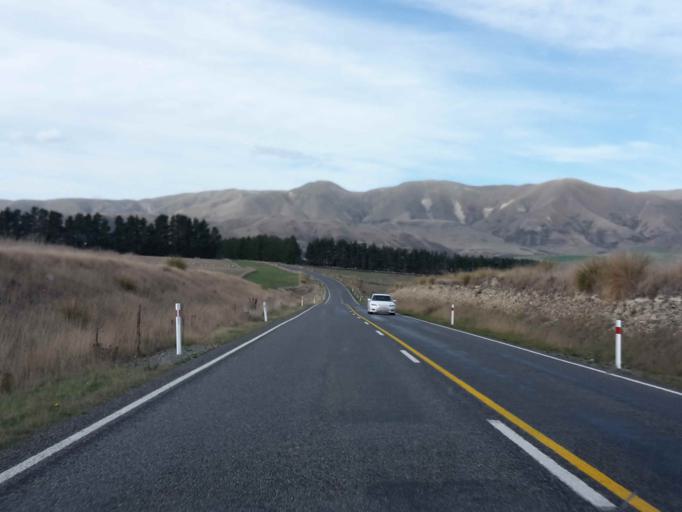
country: NZ
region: Canterbury
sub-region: Timaru District
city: Pleasant Point
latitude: -44.0917
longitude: 170.6251
